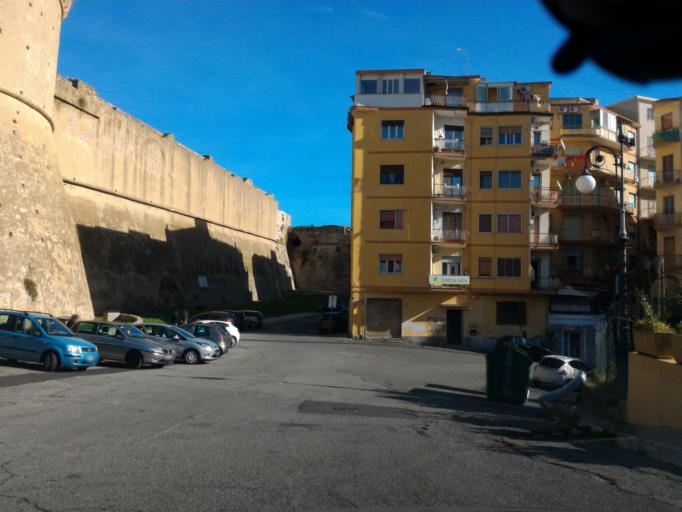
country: IT
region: Calabria
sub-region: Provincia di Crotone
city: Crotone
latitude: 39.0809
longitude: 17.1316
